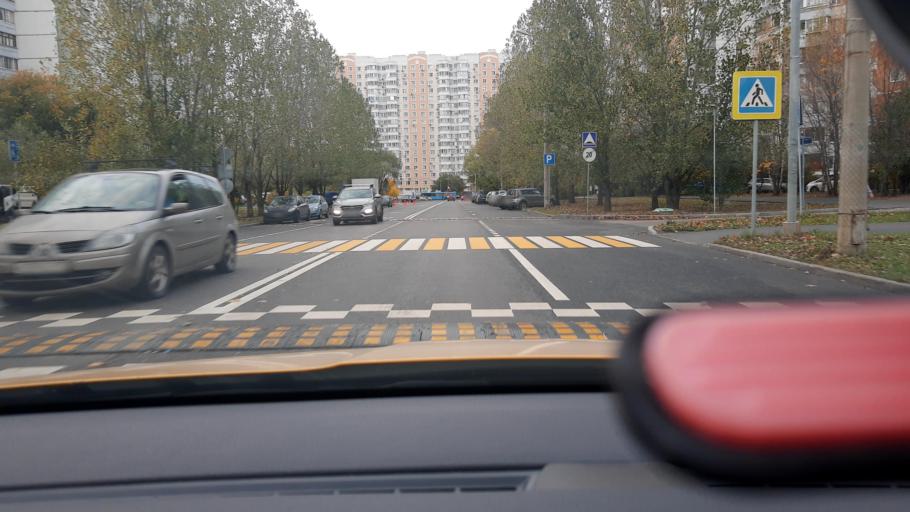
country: RU
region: Moscow
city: Novo-Peredelkino
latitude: 55.6441
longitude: 37.3427
